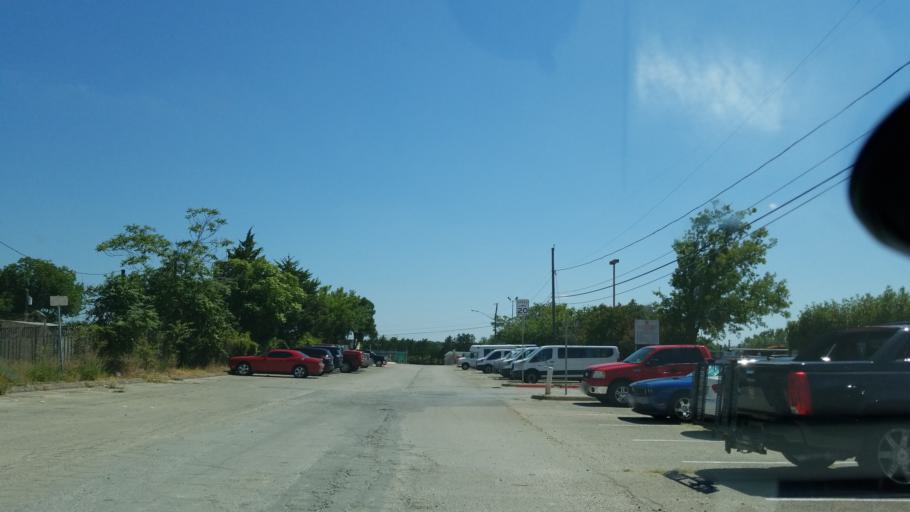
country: US
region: Texas
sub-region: Dallas County
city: Cockrell Hill
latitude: 32.7183
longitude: -96.8857
